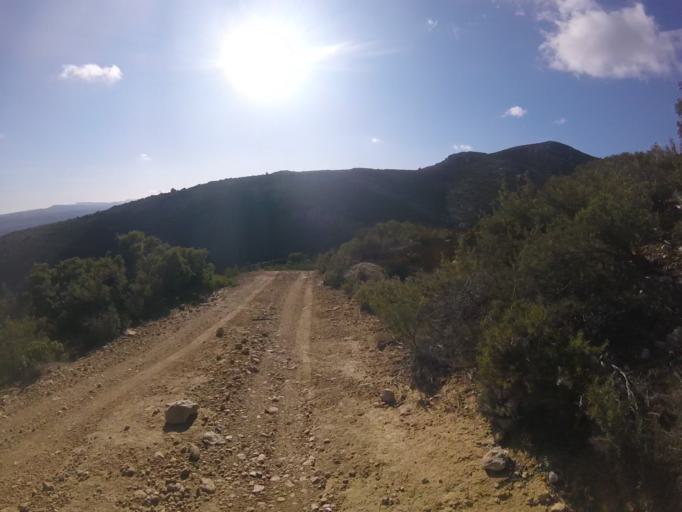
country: ES
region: Valencia
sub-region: Provincia de Castello
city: Sarratella
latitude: 40.2965
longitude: 0.0428
